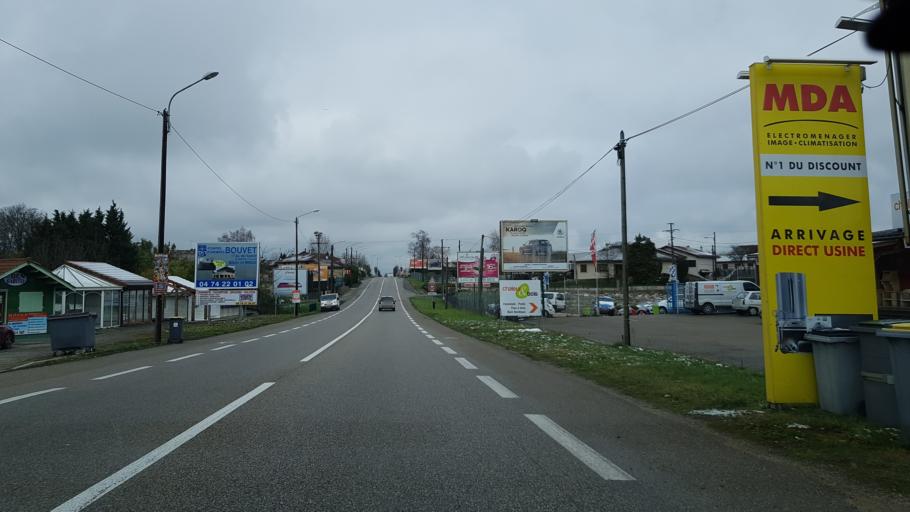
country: FR
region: Rhone-Alpes
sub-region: Departement de l'Ain
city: Peronnas
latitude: 46.1728
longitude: 5.1980
